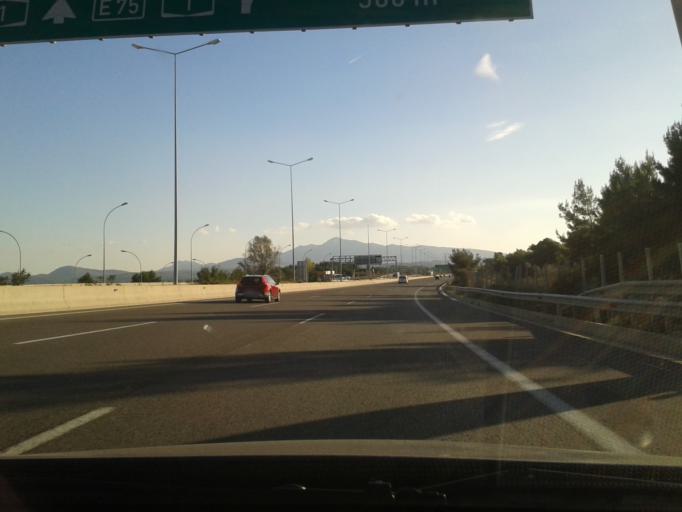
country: GR
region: Attica
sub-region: Nomarchia Anatolikis Attikis
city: Polydendri
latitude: 38.2110
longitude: 23.8550
